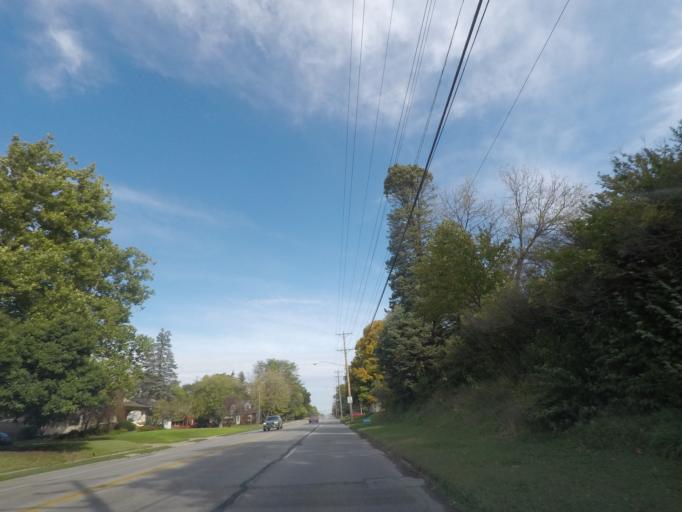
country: US
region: Iowa
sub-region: Story County
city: Ames
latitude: 42.0375
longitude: -93.6204
